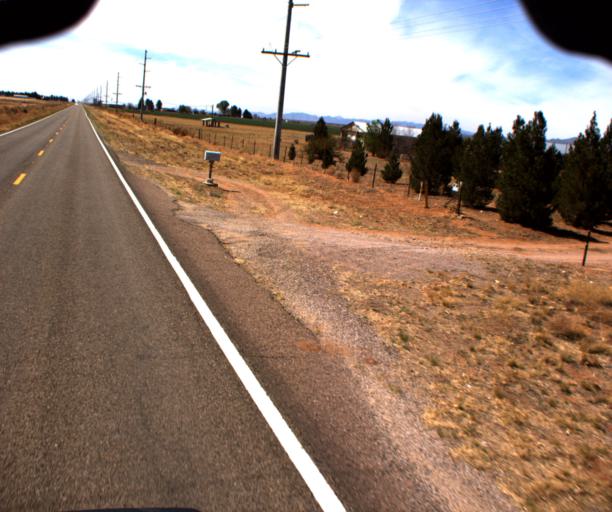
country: US
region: Arizona
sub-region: Cochise County
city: Tombstone
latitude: 31.8475
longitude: -109.6952
